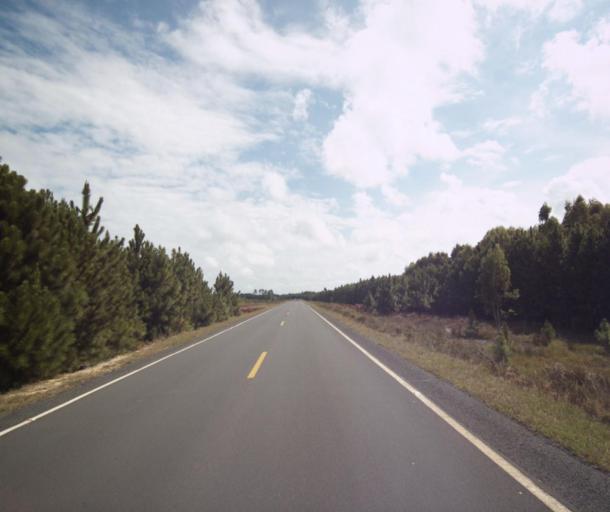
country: BR
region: Rio Grande do Sul
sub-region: Sao Lourenco Do Sul
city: Sao Lourenco do Sul
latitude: -31.4606
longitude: -51.2269
